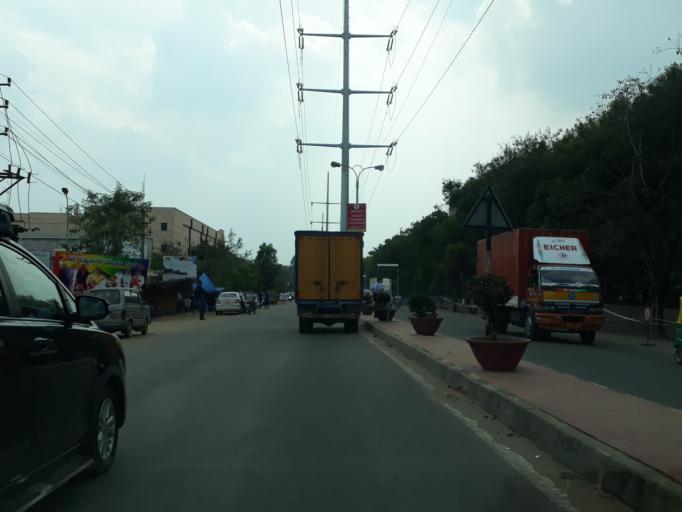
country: IN
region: Karnataka
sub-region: Bangalore Urban
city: Anekal
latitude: 12.8079
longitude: 77.6638
